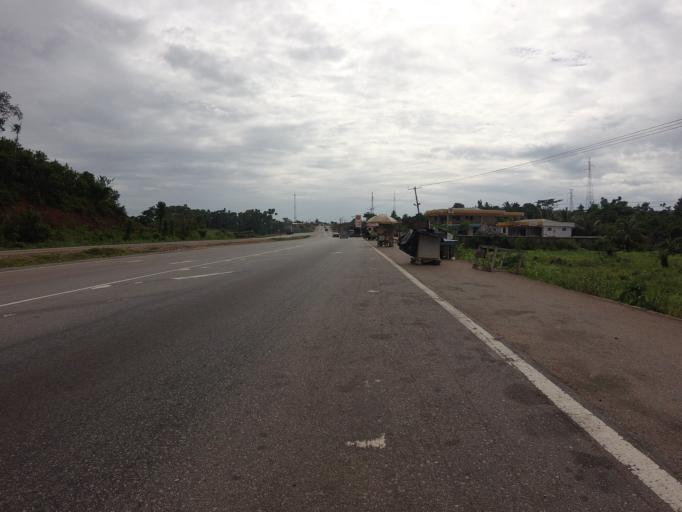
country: GH
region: Eastern
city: Nkawkaw
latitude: 6.5976
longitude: -0.8345
